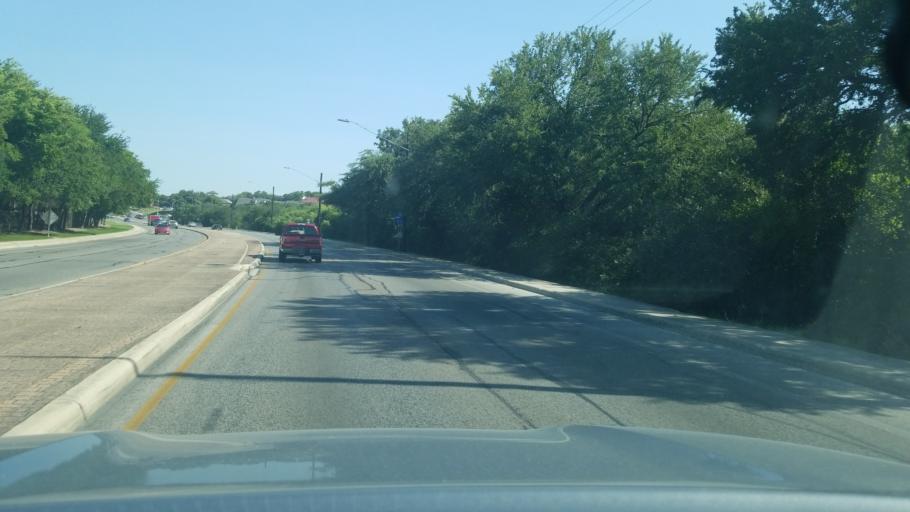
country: US
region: Texas
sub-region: Bexar County
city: Hollywood Park
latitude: 29.5830
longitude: -98.5160
